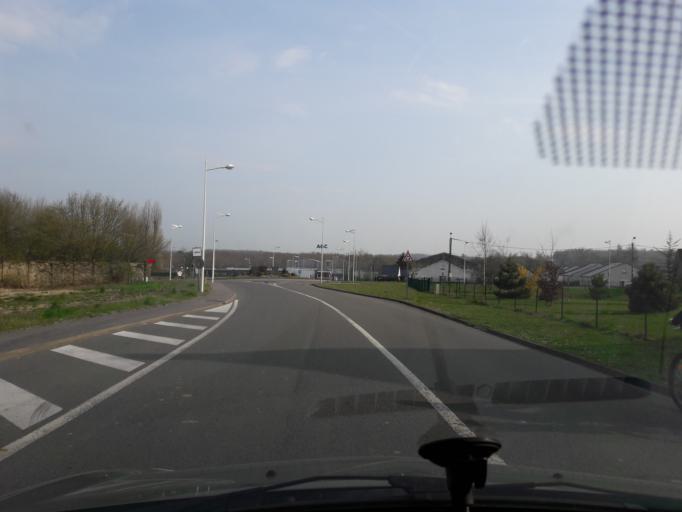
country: FR
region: Nord-Pas-de-Calais
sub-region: Departement du Nord
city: Recquignies
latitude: 50.2869
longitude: 4.0267
